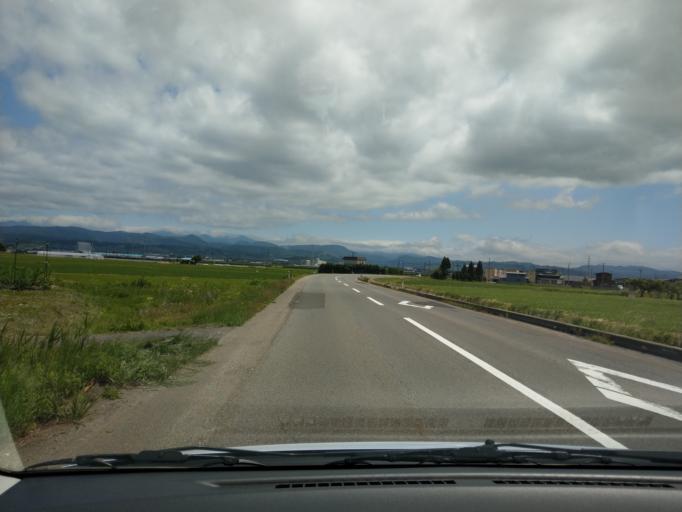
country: JP
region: Aomori
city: Kuroishi
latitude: 40.6613
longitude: 140.5587
